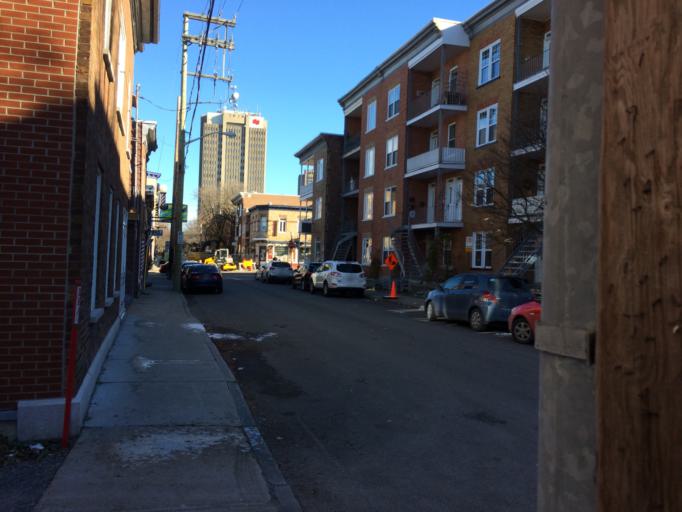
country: CA
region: Quebec
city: Quebec
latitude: 46.8045
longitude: -71.2279
